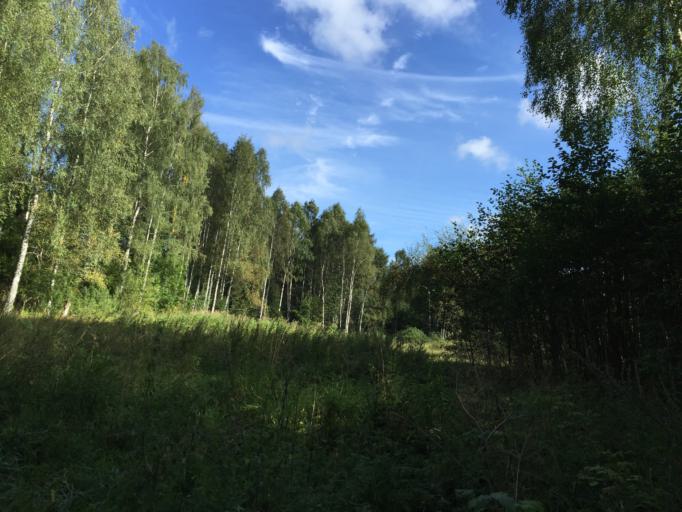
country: LV
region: Kuldigas Rajons
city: Kuldiga
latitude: 57.0067
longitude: 21.7790
